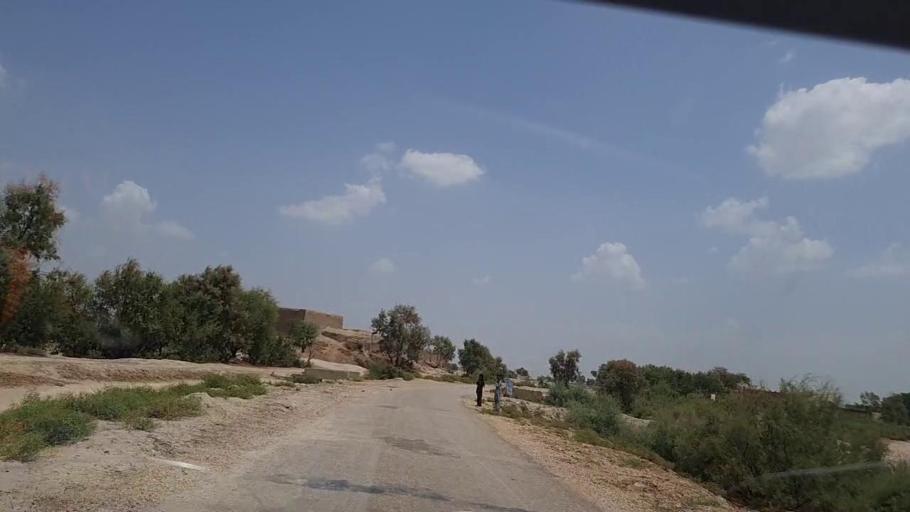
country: PK
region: Sindh
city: Bhan
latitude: 26.5212
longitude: 67.6360
